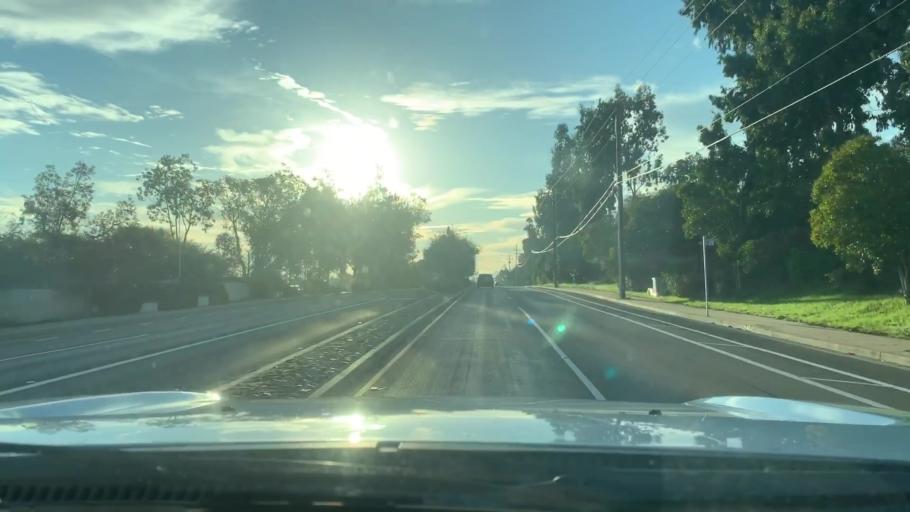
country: US
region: California
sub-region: San Luis Obispo County
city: San Luis Obispo
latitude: 35.2647
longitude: -120.6999
